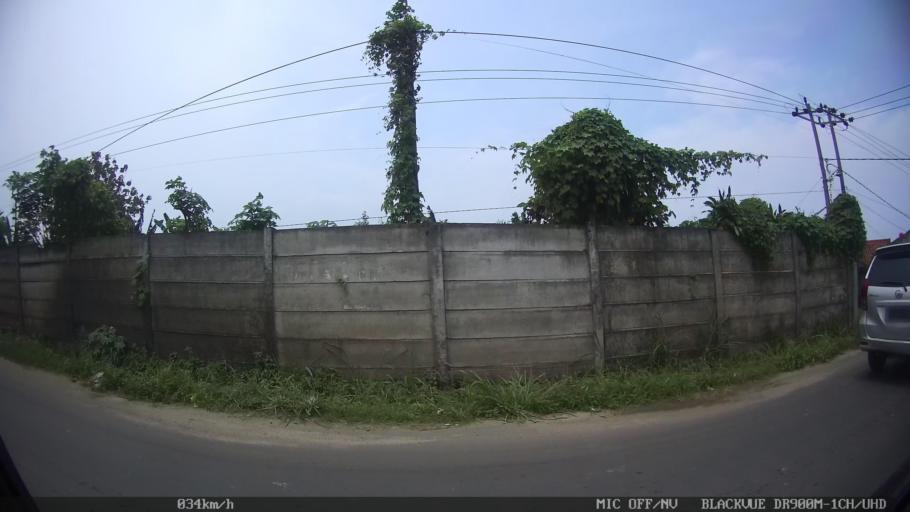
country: ID
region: Lampung
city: Bandarlampung
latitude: -5.4182
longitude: 105.2860
